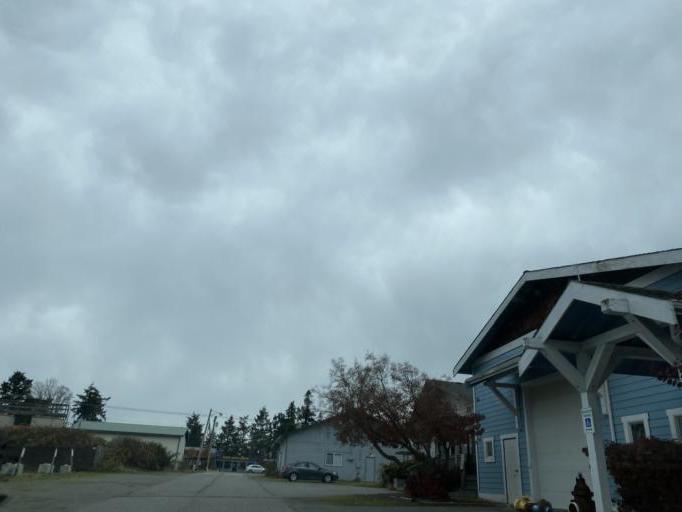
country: US
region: Washington
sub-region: Island County
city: Freeland
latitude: 48.0086
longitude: -122.5256
